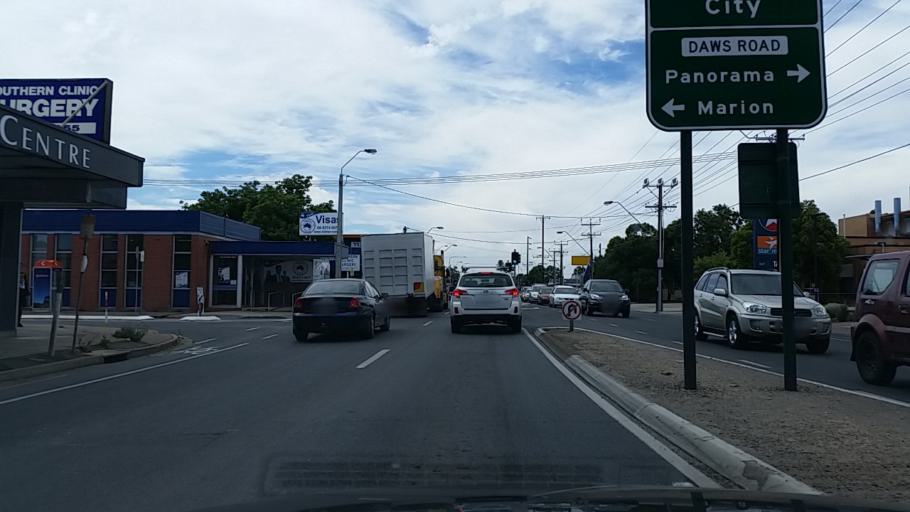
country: AU
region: South Australia
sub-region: Marion
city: Clovelly Park
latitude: -34.9947
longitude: 138.5750
